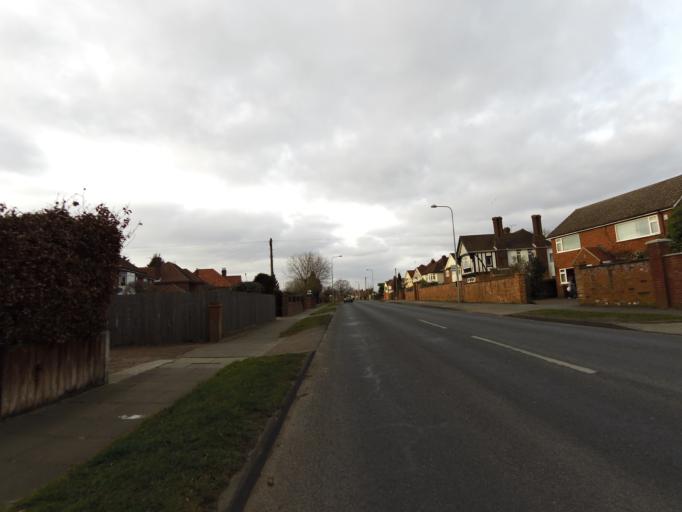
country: GB
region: England
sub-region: Suffolk
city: Ipswich
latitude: 52.0753
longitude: 1.1518
